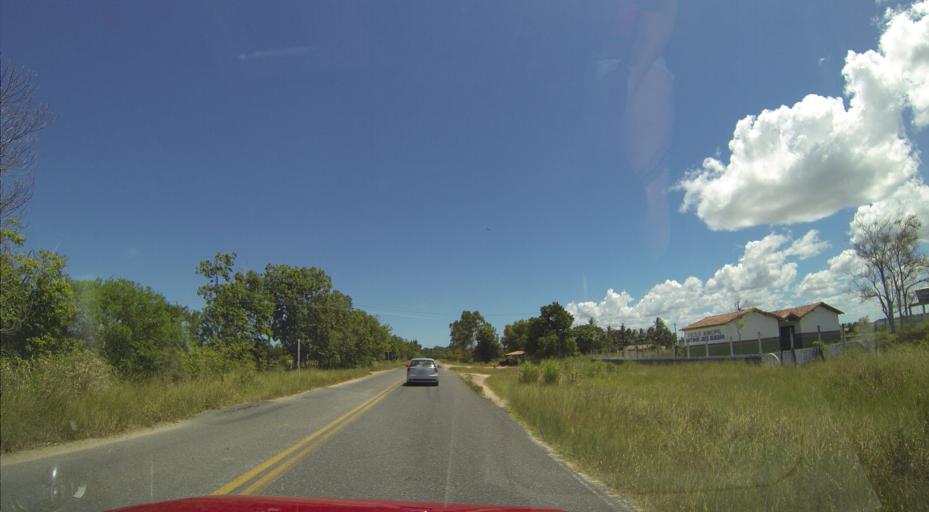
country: BR
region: Bahia
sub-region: Prado
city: Prado
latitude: -17.2128
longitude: -39.3877
